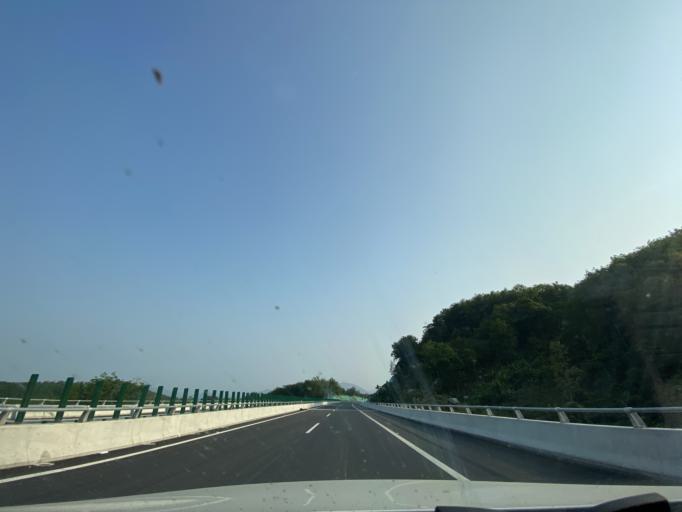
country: CN
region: Hainan
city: Xiangshui
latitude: 18.6507
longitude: 109.6290
